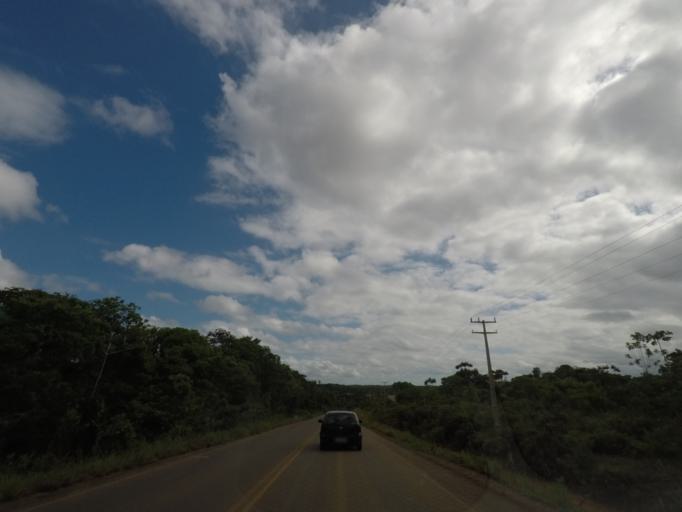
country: BR
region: Bahia
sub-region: Itacare
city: Itacare
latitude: -14.2075
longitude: -39.1009
